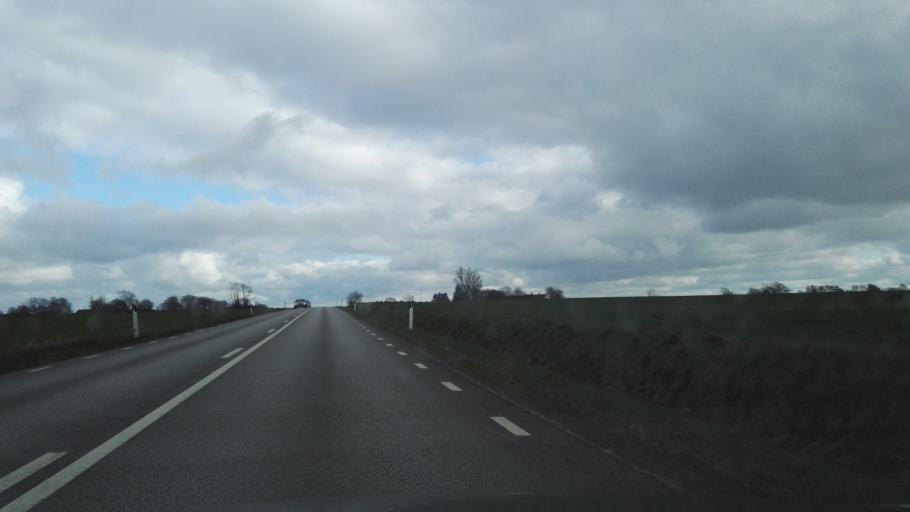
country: SE
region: Skane
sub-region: Horby Kommun
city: Hoerby
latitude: 55.7553
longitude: 13.6830
